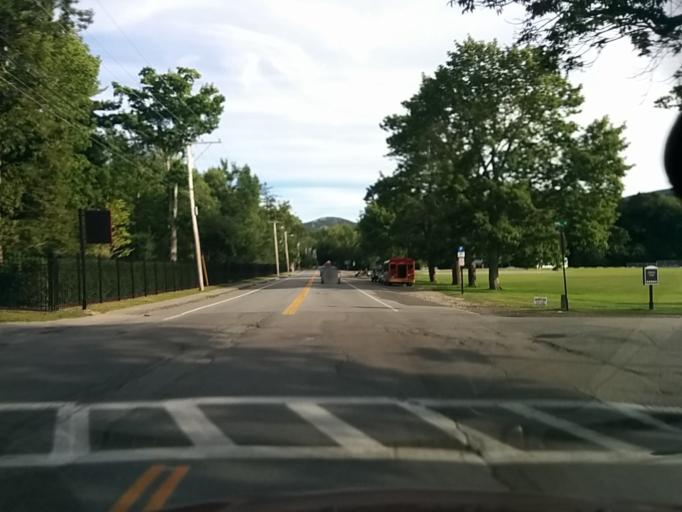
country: US
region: Maine
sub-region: Hancock County
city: Bar Harbor
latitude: 44.3831
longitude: -68.2031
